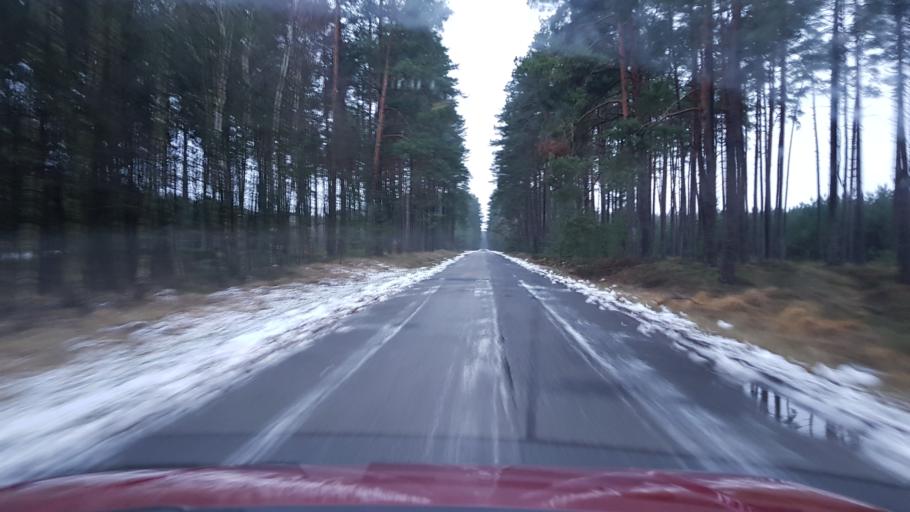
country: PL
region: West Pomeranian Voivodeship
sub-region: Powiat goleniowski
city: Goleniow
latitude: 53.4814
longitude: 14.8457
